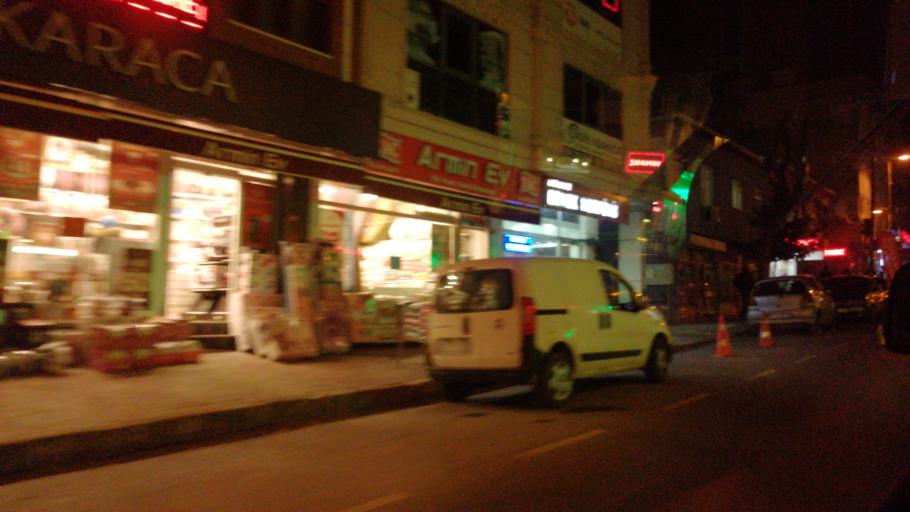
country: TR
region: Istanbul
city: Umraniye
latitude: 41.0125
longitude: 29.1281
